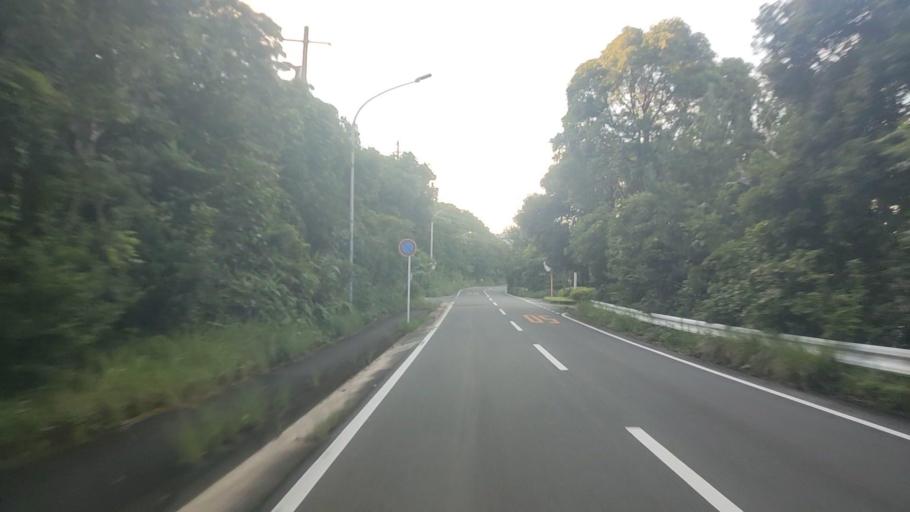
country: JP
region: Mie
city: Toba
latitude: 34.3158
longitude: 136.8157
